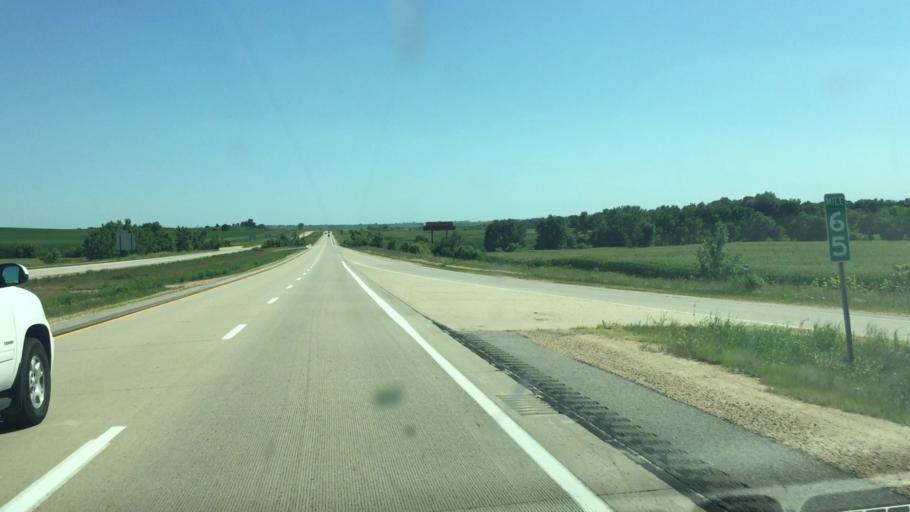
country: US
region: Iowa
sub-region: Jones County
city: Monticello
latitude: 42.2267
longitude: -91.1719
